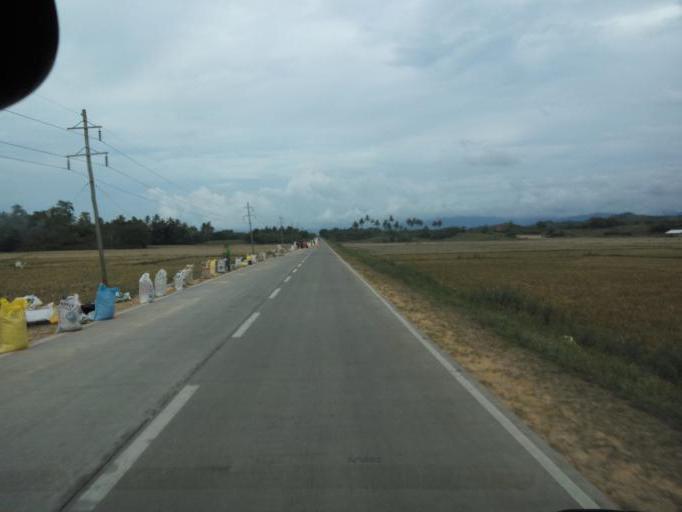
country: PH
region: Cagayan Valley
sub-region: Province of Cagayan
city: Santa Teresita
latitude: 18.2390
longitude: 121.9061
